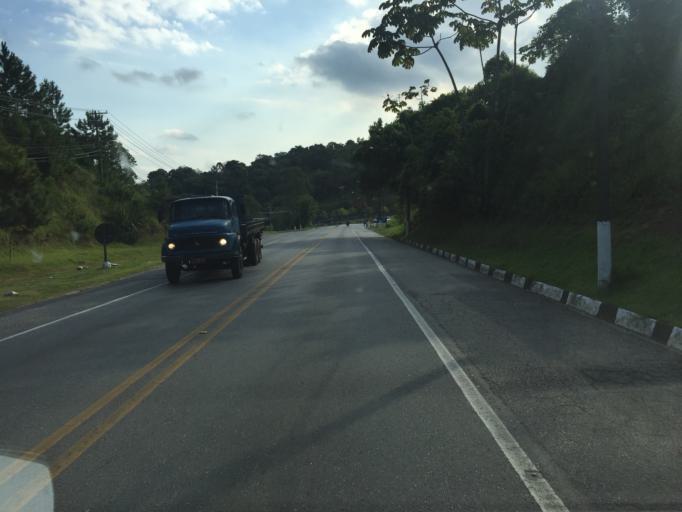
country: BR
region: Sao Paulo
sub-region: Aruja
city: Aruja
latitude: -23.4037
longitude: -46.3135
